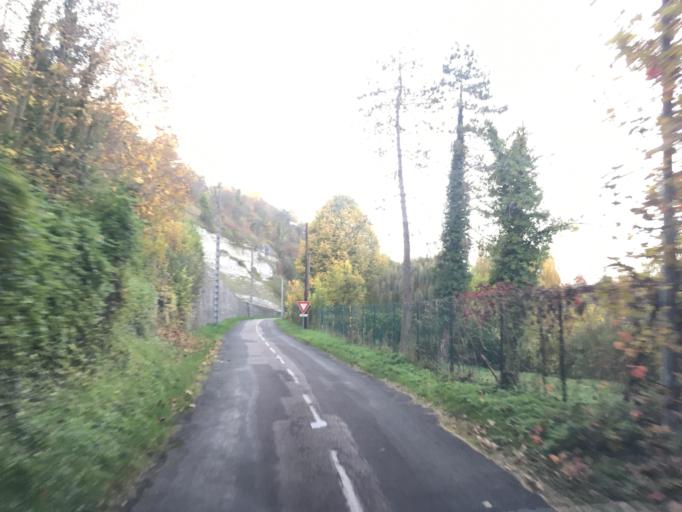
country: FR
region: Haute-Normandie
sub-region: Departement de l'Eure
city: Heudreville-sur-Eure
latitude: 49.1134
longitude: 1.2088
